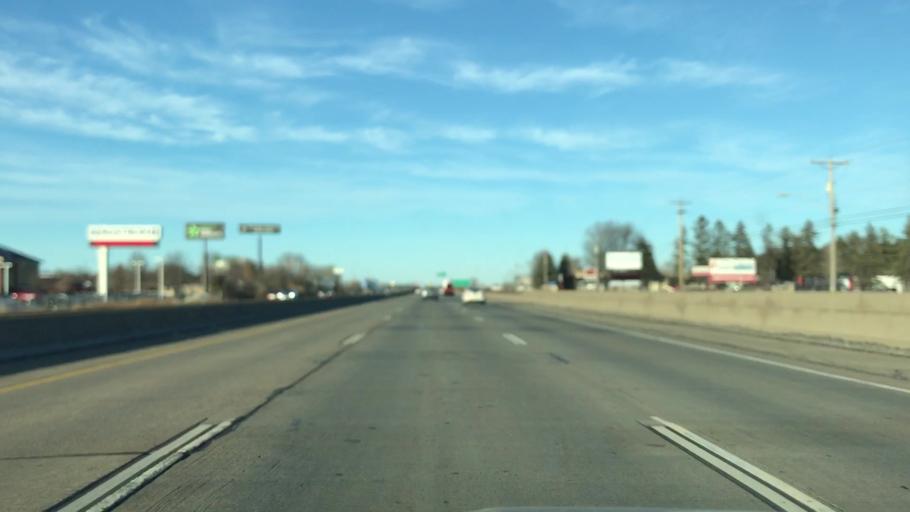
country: US
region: Wisconsin
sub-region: Outagamie County
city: Appleton
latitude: 44.2531
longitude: -88.4663
